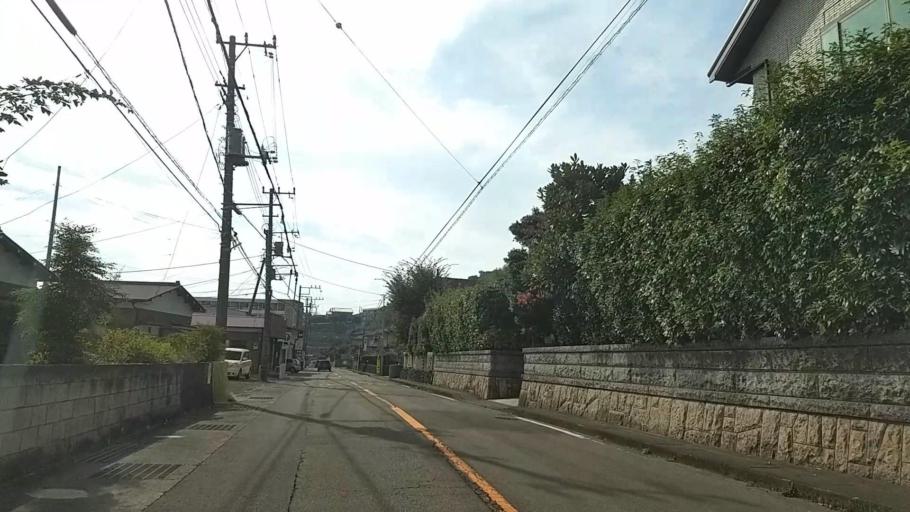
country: JP
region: Kanagawa
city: Atsugi
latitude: 35.4502
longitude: 139.3519
